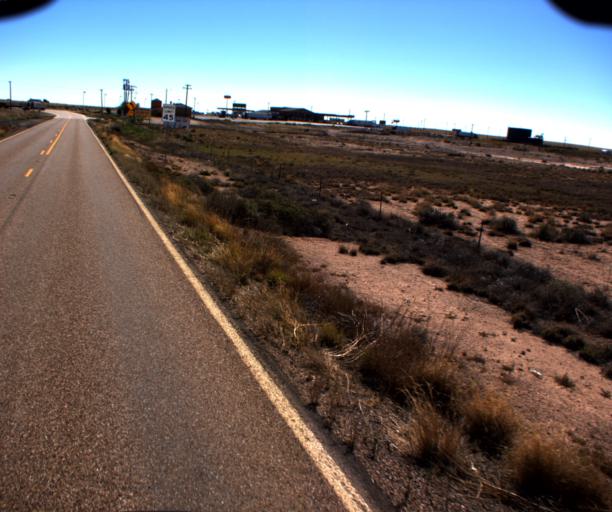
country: US
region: Arizona
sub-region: Navajo County
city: Holbrook
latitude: 34.9784
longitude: -110.0886
